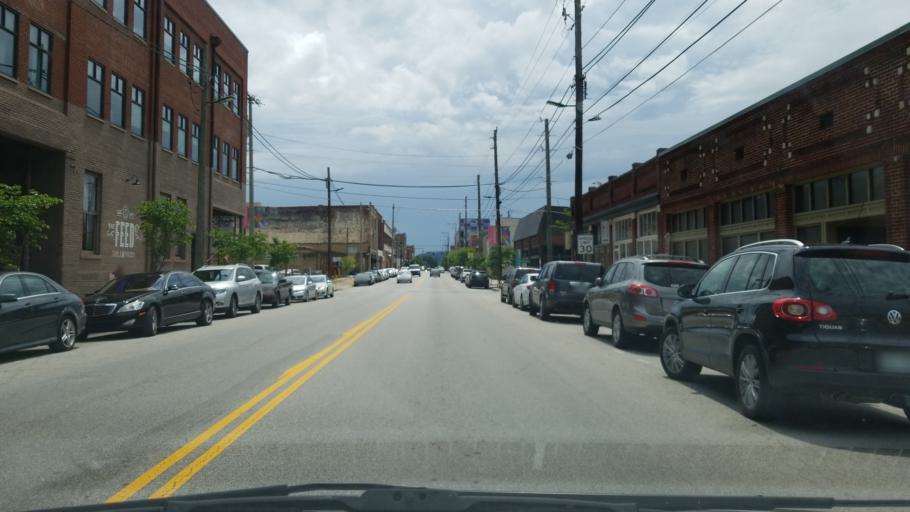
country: US
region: Tennessee
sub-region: Hamilton County
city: Chattanooga
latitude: 35.0371
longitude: -85.3098
